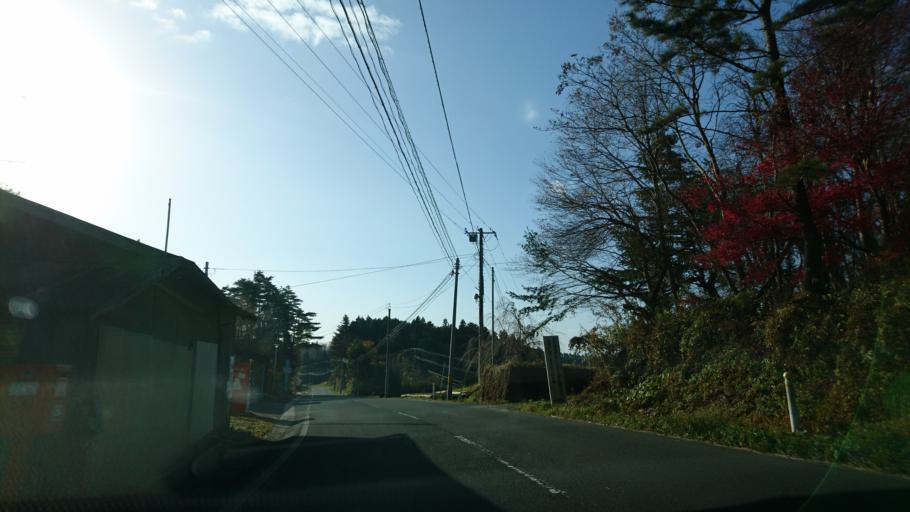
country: JP
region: Iwate
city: Ichinoseki
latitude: 38.8800
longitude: 141.2914
